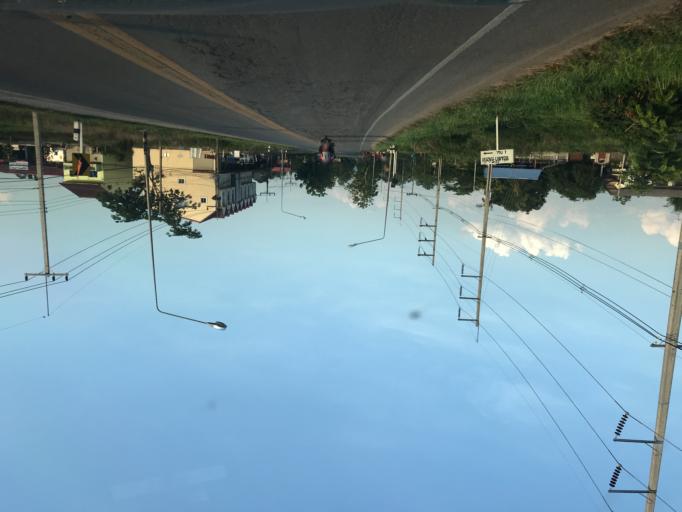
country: TH
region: Phayao
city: Chiang Kham
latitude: 19.5357
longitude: 100.2909
